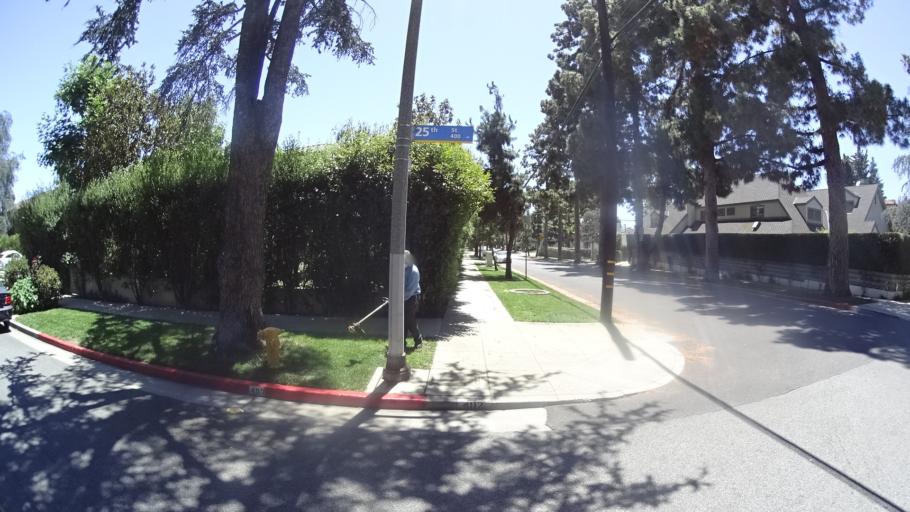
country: US
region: California
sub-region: Los Angeles County
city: Santa Monica
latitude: 34.0450
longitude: -118.4897
